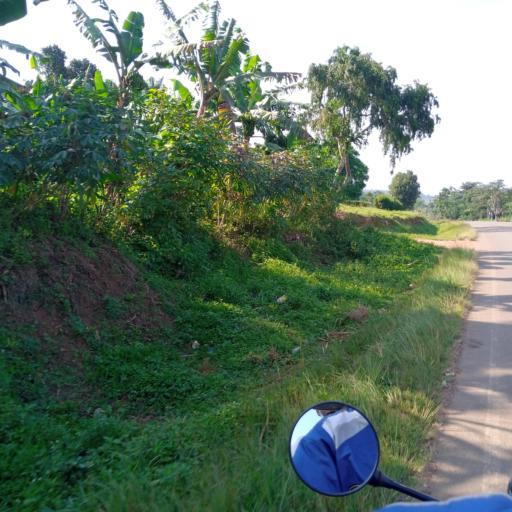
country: UG
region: Central Region
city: Masaka
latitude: -0.4369
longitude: 31.6625
